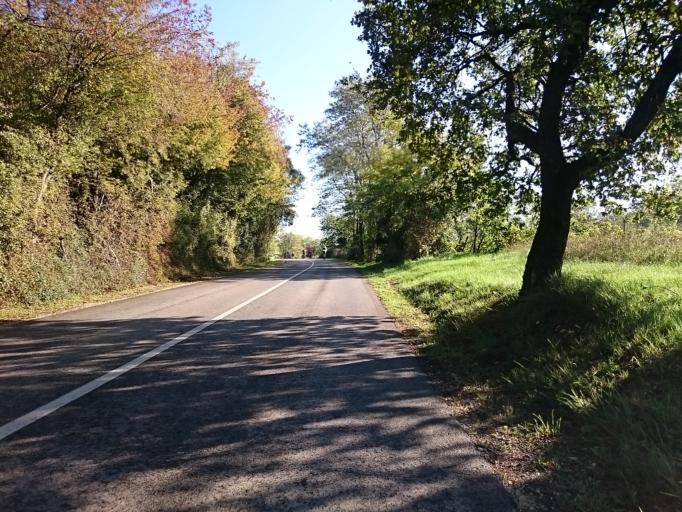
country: HR
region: Istarska
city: Novigrad
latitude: 45.3637
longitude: 13.5980
